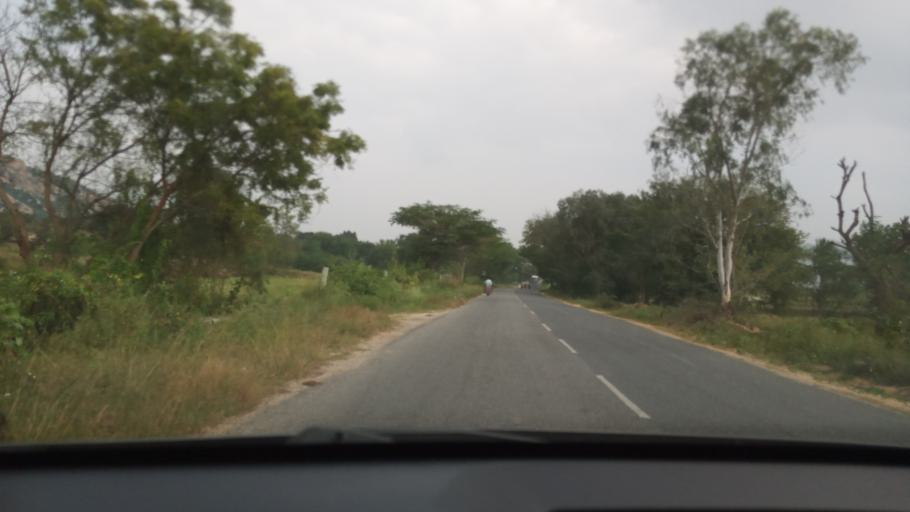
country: IN
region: Andhra Pradesh
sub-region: Chittoor
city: Pakala
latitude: 13.6561
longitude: 78.8525
